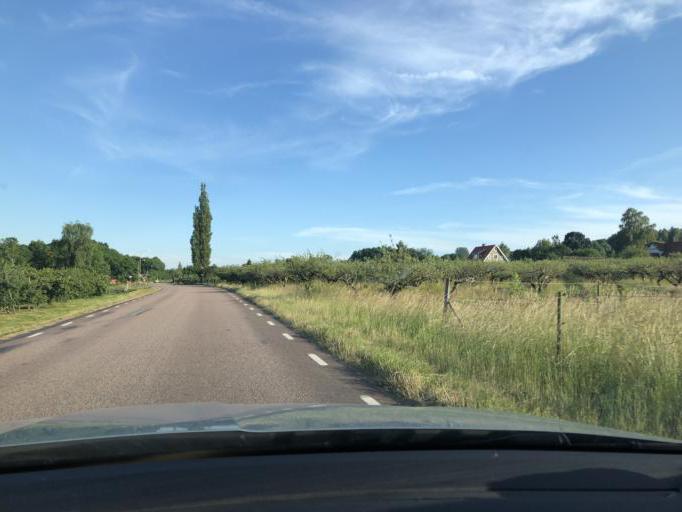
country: SE
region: Blekinge
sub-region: Solvesborgs Kommun
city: Soelvesborg
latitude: 56.1557
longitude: 14.6009
